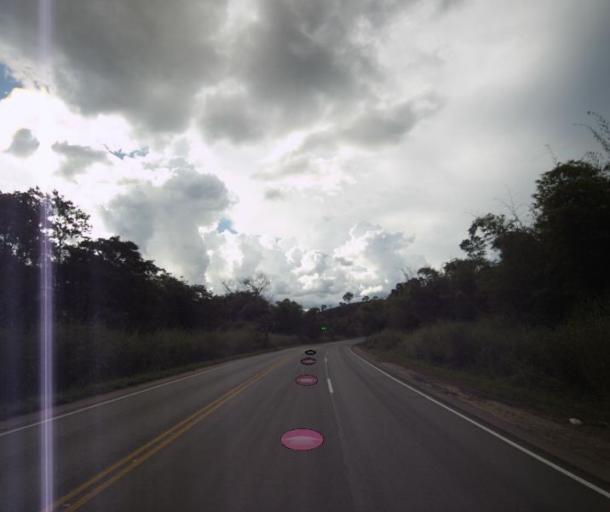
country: BR
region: Goias
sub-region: Rialma
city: Rialma
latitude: -15.2505
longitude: -49.5558
